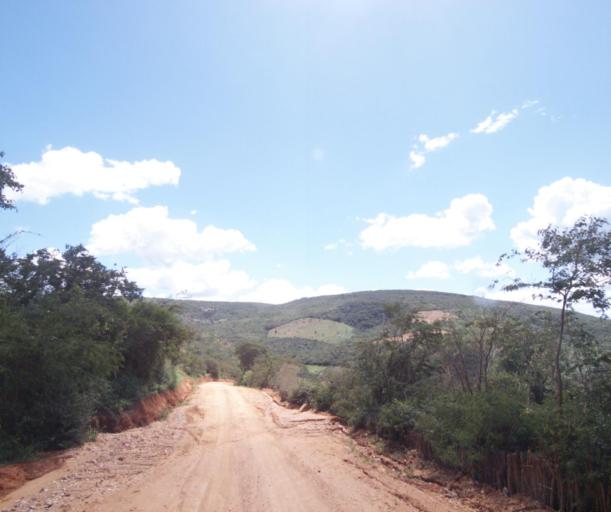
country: BR
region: Bahia
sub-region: Pocoes
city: Pocoes
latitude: -14.2947
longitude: -40.6821
